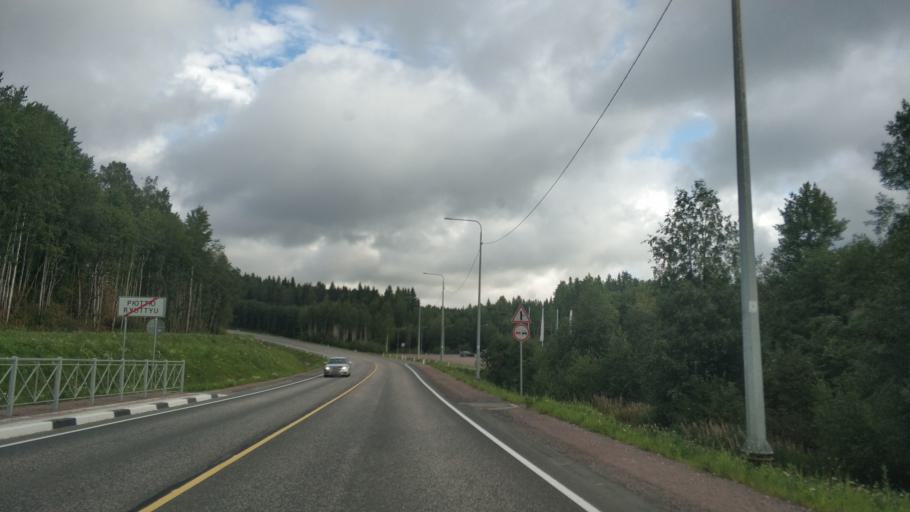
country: RU
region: Republic of Karelia
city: Khelyulya
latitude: 61.8232
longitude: 30.6350
